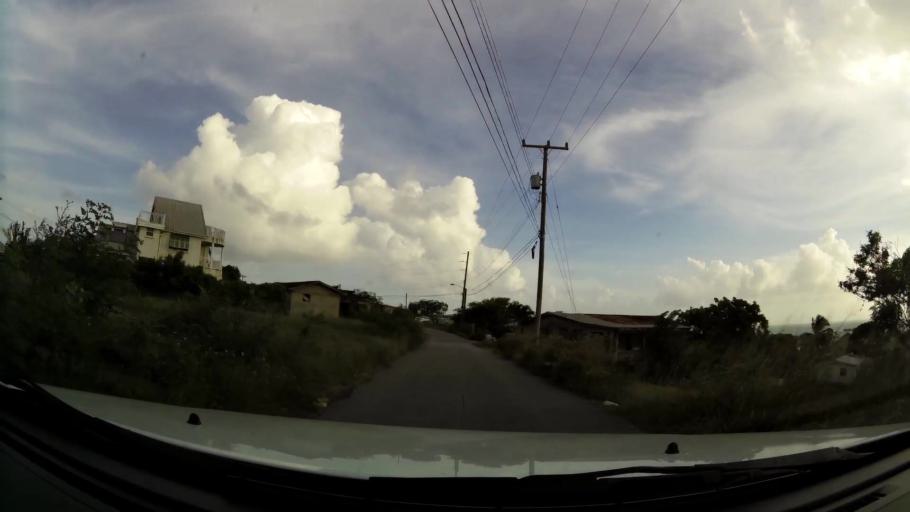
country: BB
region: Christ Church
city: Oistins
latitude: 13.0672
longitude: -59.5331
